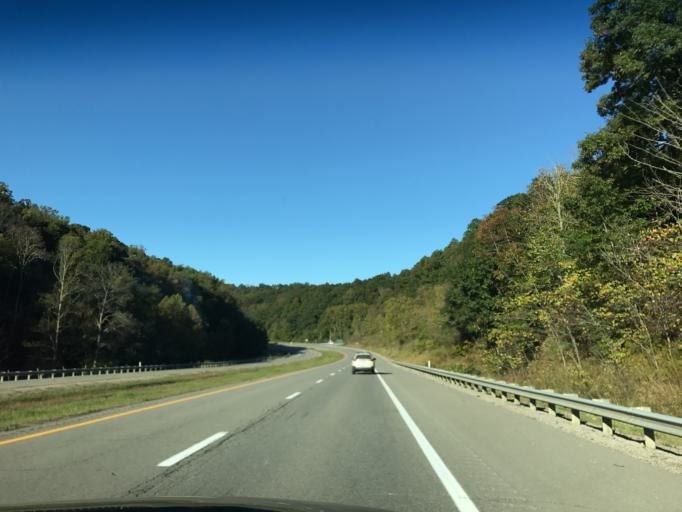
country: US
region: Ohio
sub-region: Washington County
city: Newport
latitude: 39.2592
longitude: -81.2868
